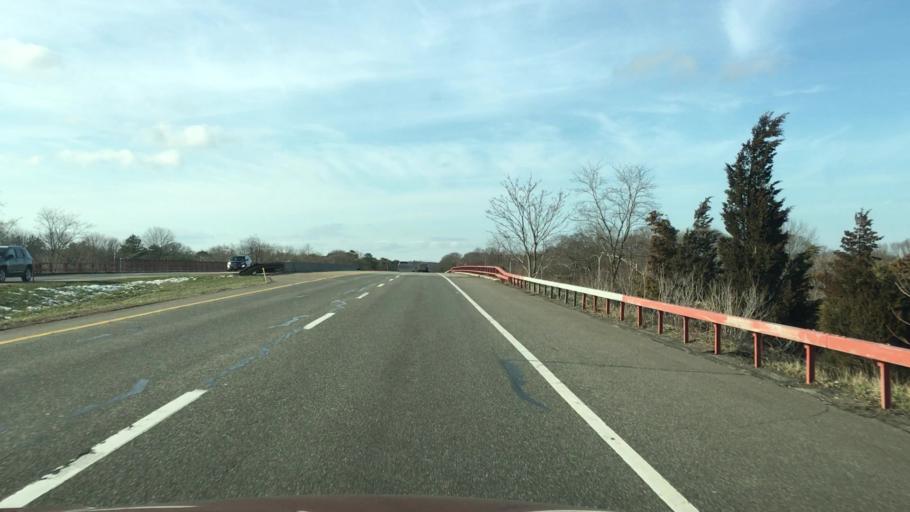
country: US
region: New York
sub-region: Suffolk County
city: Centereach
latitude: 40.8597
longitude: -73.0682
